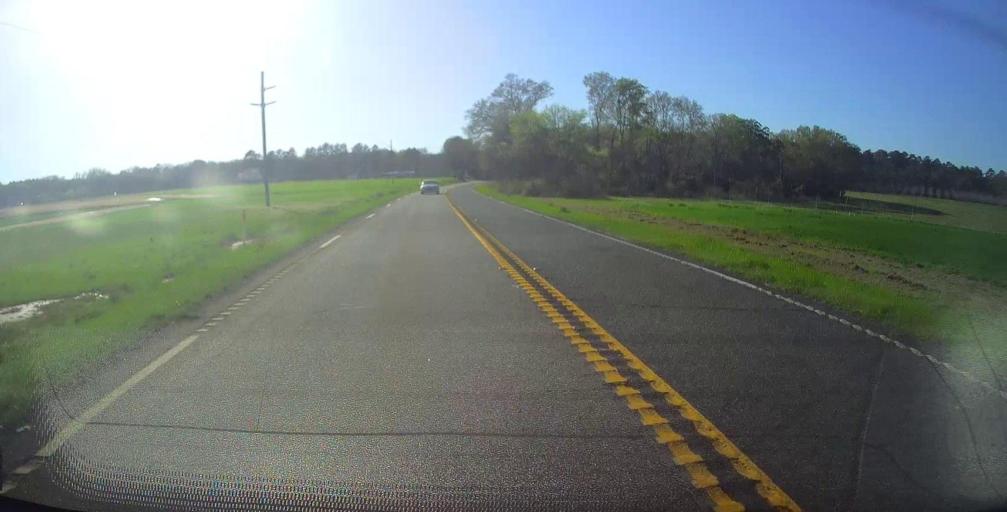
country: US
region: Georgia
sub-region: Macon County
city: Marshallville
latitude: 32.4395
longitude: -83.8818
